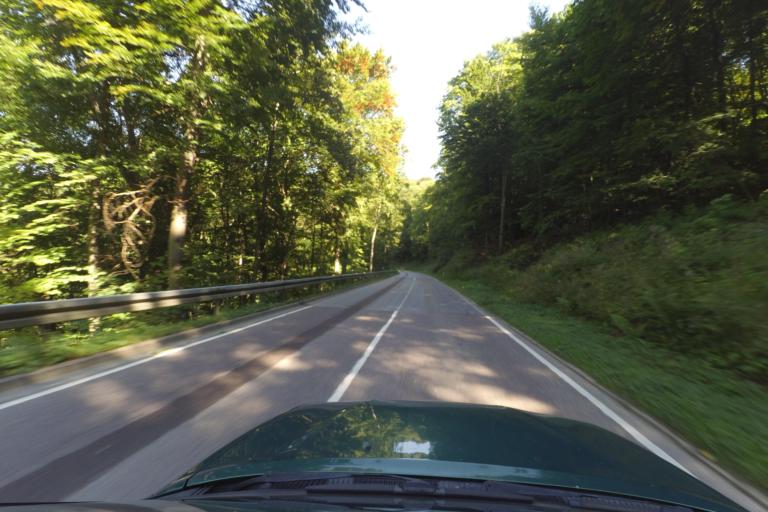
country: DE
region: Baden-Wuerttemberg
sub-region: Regierungsbezirk Stuttgart
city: Heubach
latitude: 48.7692
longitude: 9.9498
